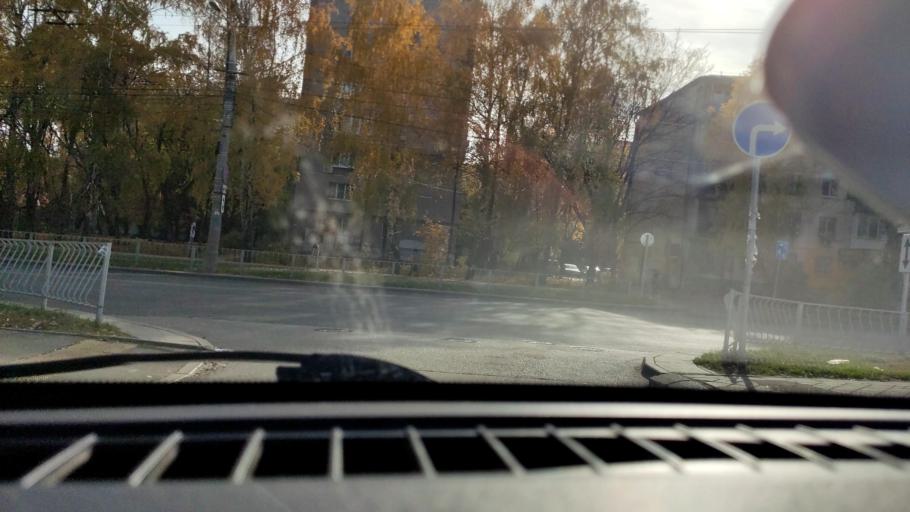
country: RU
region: Samara
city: Samara
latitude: 53.2301
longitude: 50.2092
